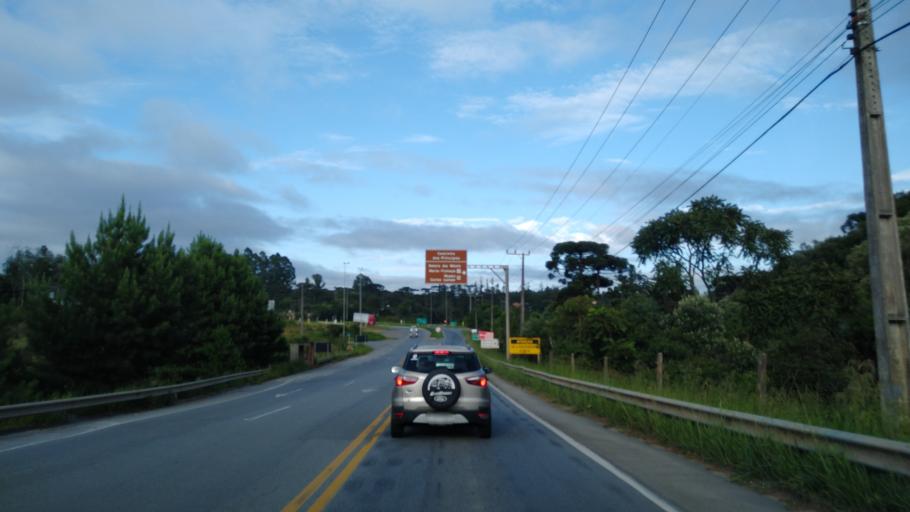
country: BR
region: Santa Catarina
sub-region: Rio Negrinho
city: Rio Negrinho
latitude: -26.2445
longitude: -49.4584
